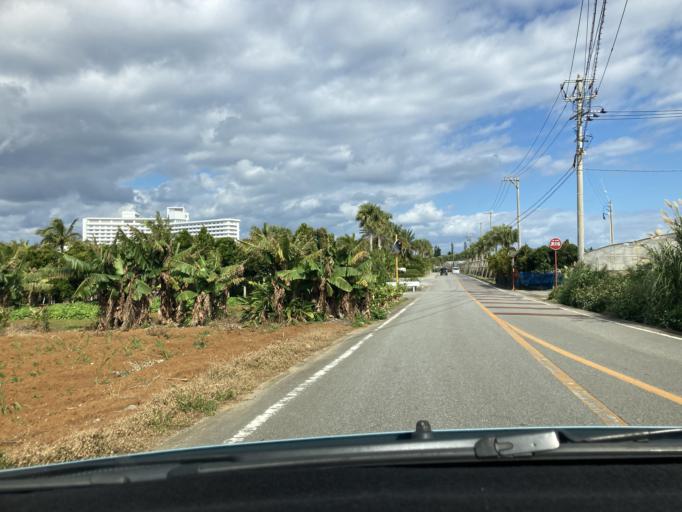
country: JP
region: Okinawa
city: Ishikawa
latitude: 26.4307
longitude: 127.7187
